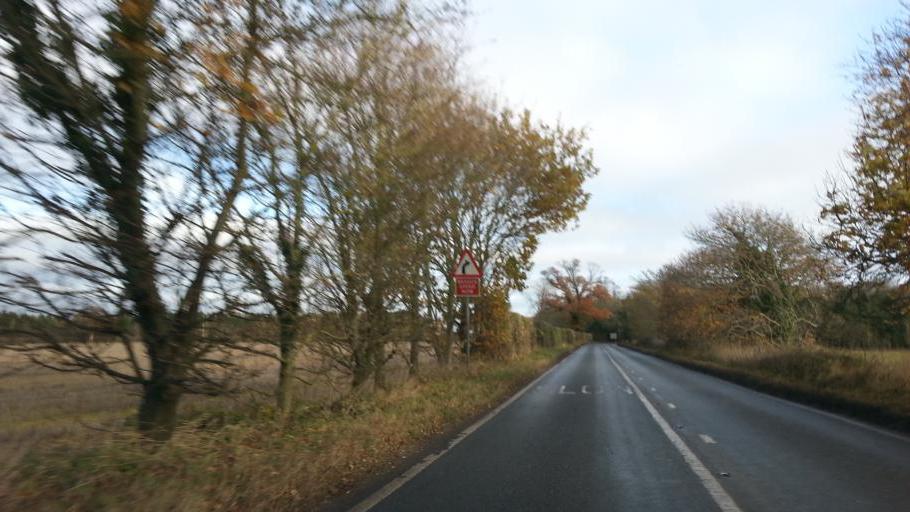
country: GB
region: England
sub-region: Suffolk
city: Wickham Market
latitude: 52.1200
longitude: 1.3887
